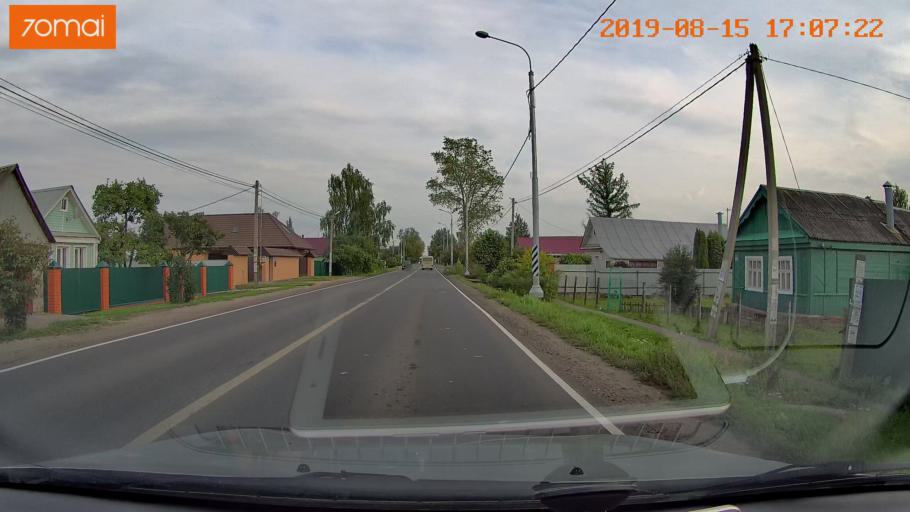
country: RU
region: Moskovskaya
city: Beloozerskiy
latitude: 55.4634
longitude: 38.4205
